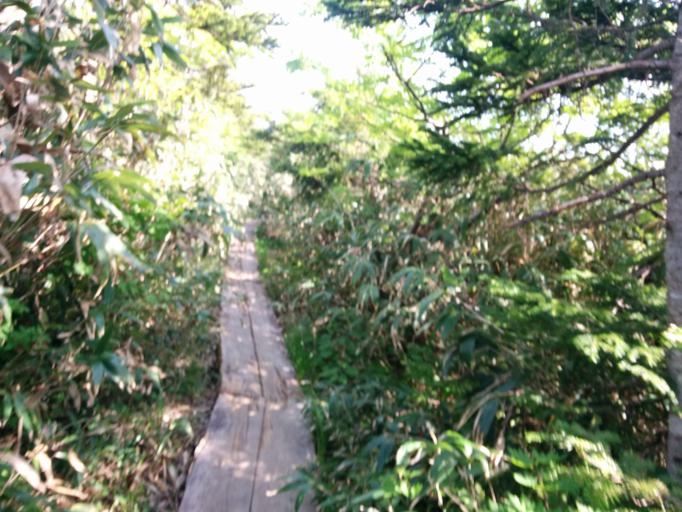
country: JP
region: Aomori
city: Aomori Shi
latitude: 40.6740
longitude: 140.8667
